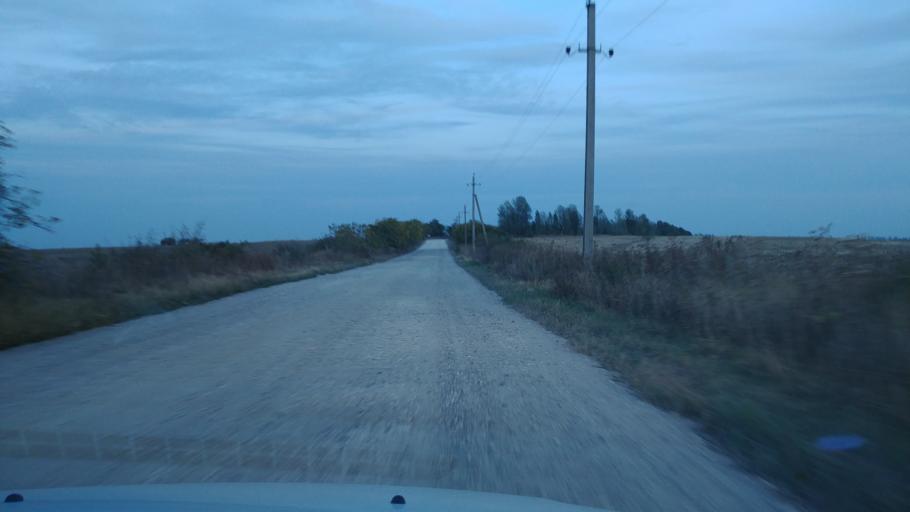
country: MD
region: Rezina
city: Saharna
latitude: 47.6810
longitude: 28.9122
